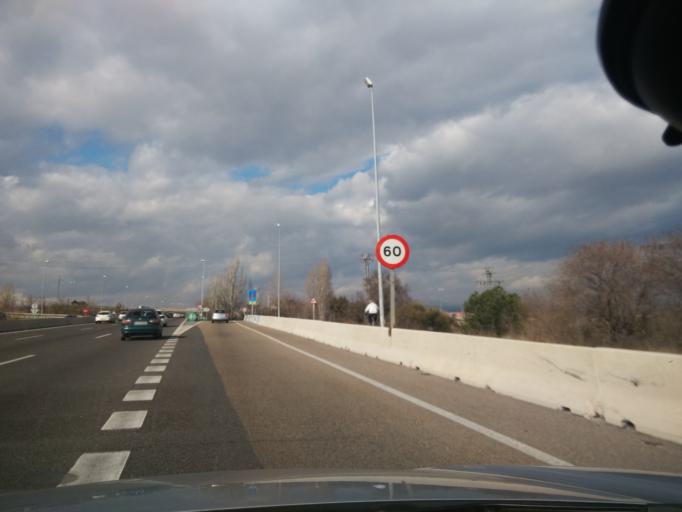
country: ES
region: Madrid
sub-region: Provincia de Madrid
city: Las Tablas
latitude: 40.5459
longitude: -3.7035
